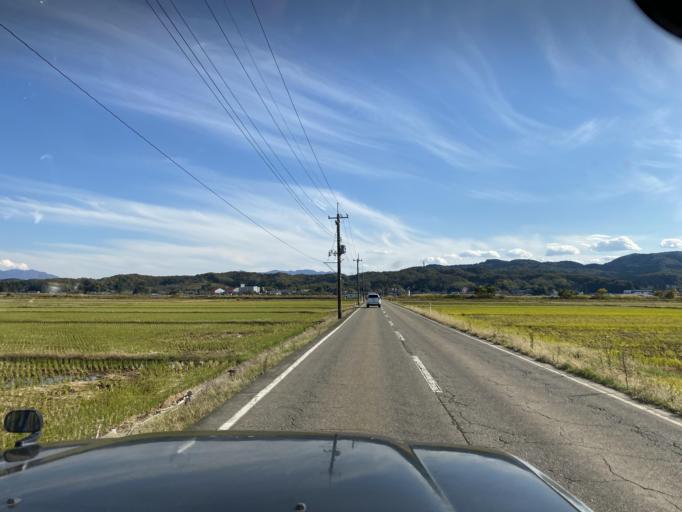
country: JP
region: Niigata
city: Niitsu-honcho
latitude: 37.7579
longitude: 139.0883
